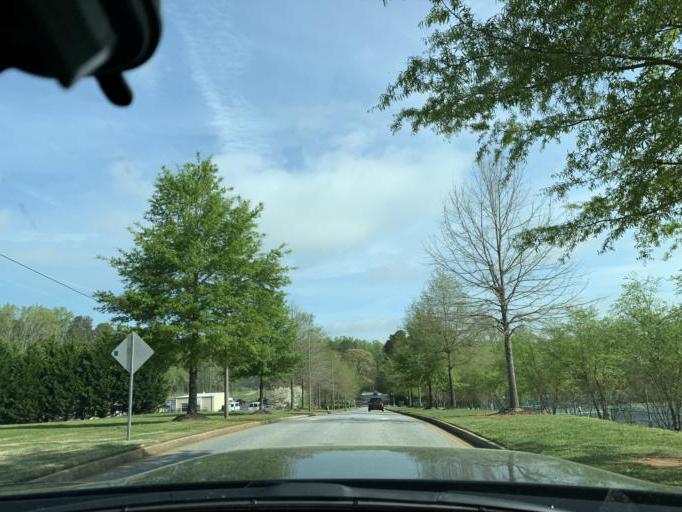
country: US
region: Georgia
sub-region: Forsyth County
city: Cumming
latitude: 34.2480
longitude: -84.1035
